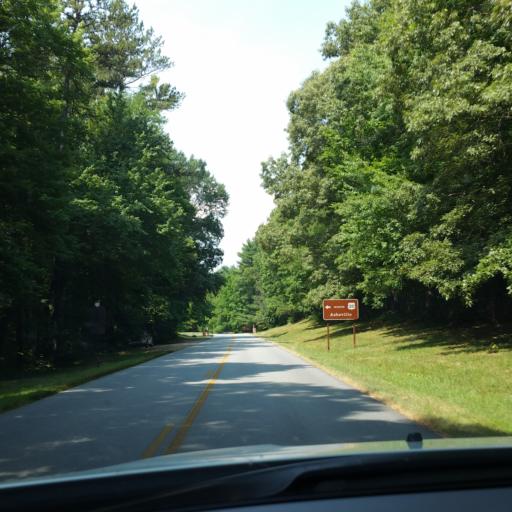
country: US
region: North Carolina
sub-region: Buncombe County
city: Biltmore Forest
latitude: 35.5213
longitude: -82.5259
